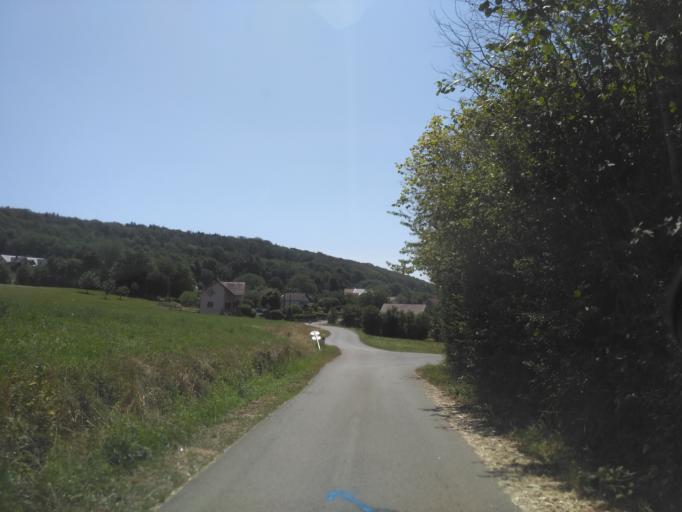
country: FR
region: Franche-Comte
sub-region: Departement de la Haute-Saone
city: Villersexel
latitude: 47.4996
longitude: 6.5290
